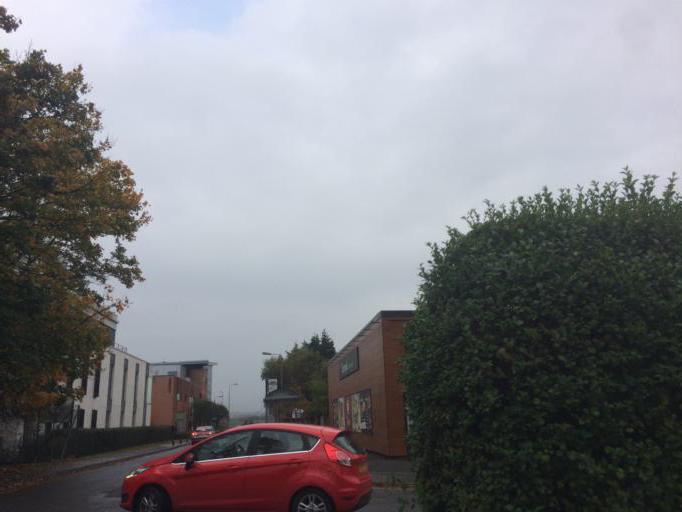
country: GB
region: Scotland
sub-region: Edinburgh
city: Newbridge
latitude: 55.9375
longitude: -3.3912
